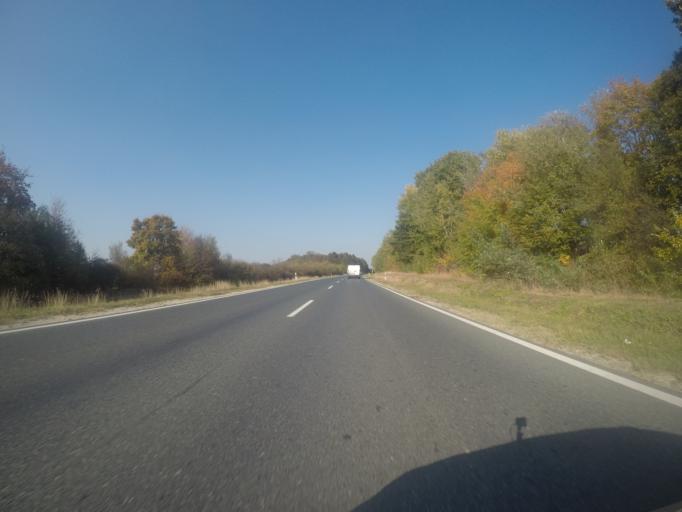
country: HU
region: Tolna
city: Bolcske
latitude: 46.7318
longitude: 18.8824
